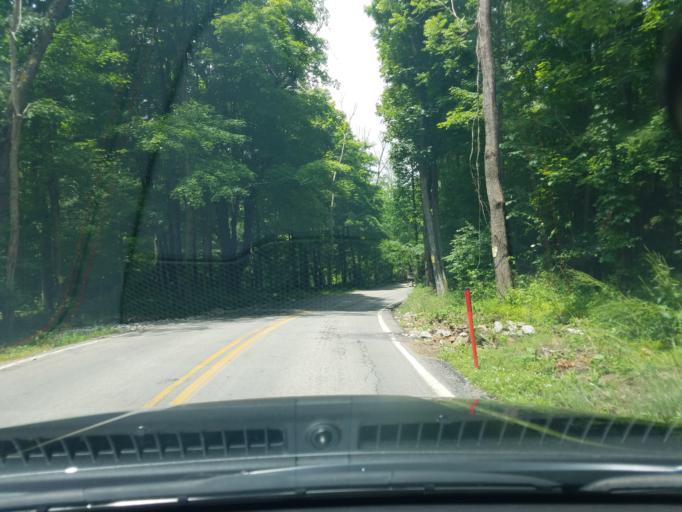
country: US
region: Pennsylvania
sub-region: Fayette County
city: Bear Rocks
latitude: 40.1629
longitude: -79.3525
